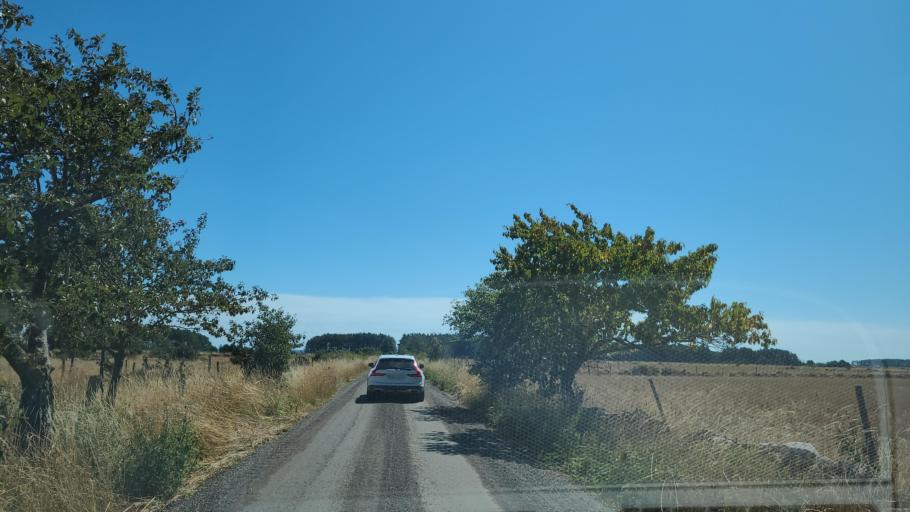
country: SE
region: Kalmar
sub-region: Morbylanga Kommun
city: Sodra Sandby
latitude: 56.7091
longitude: 16.7256
